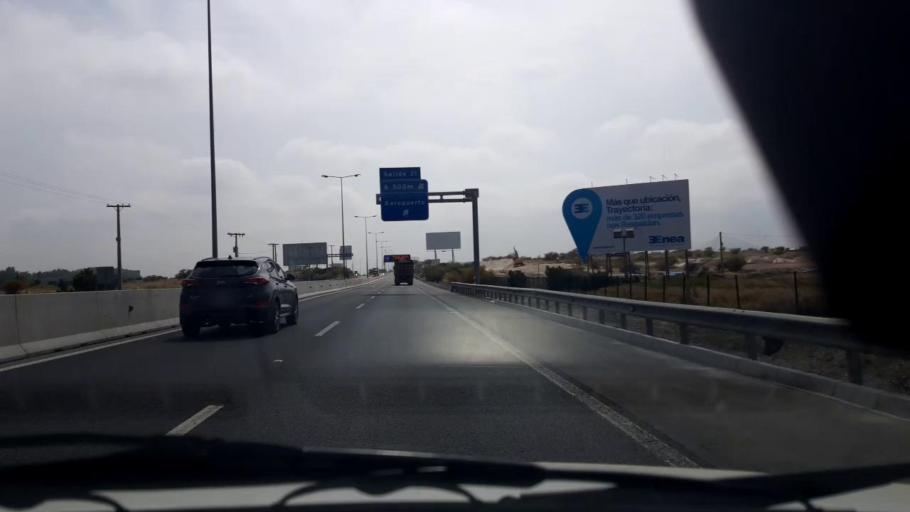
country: CL
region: Santiago Metropolitan
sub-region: Provincia de Santiago
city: Lo Prado
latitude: -33.4234
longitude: -70.7975
